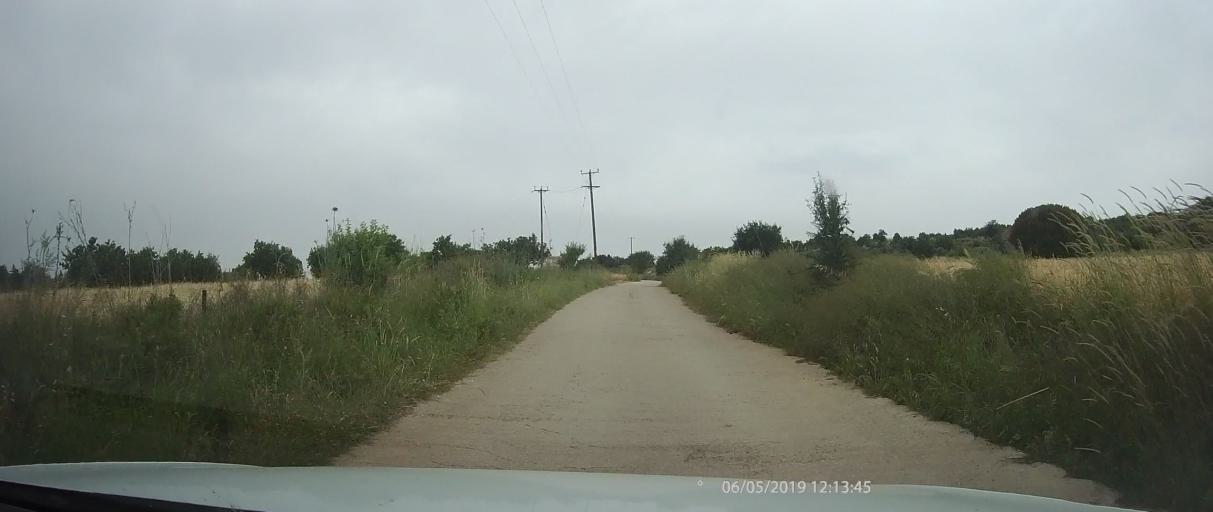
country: CY
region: Pafos
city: Tala
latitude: 34.8428
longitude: 32.4225
